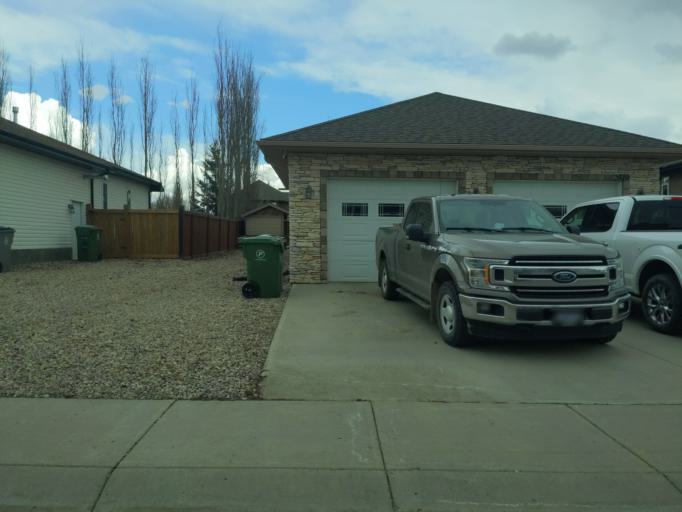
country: CA
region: Saskatchewan
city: Lloydminster
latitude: 53.2653
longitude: -110.0401
